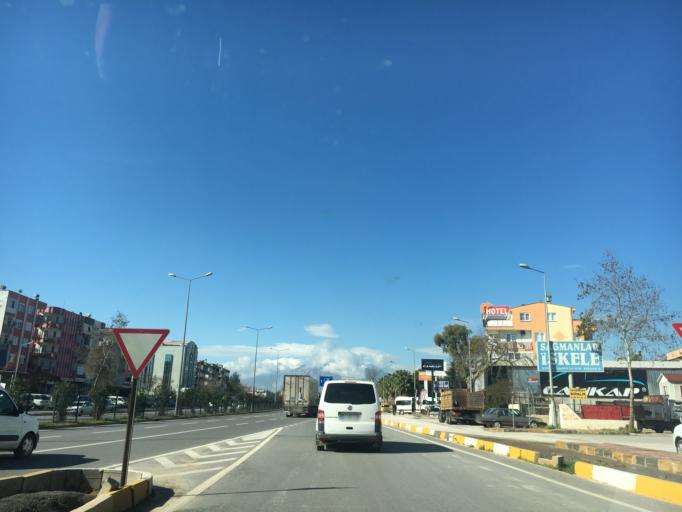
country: TR
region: Antalya
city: Antalya
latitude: 36.9122
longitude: 30.7022
